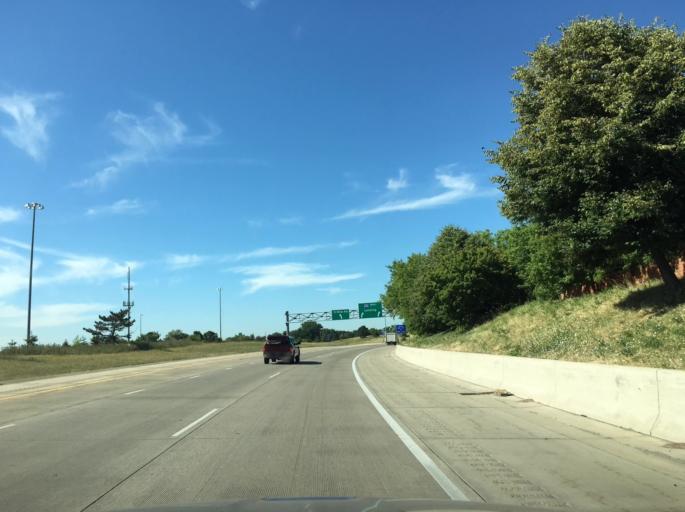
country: US
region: Michigan
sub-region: Macomb County
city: Roseville
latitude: 42.4993
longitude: -82.9184
